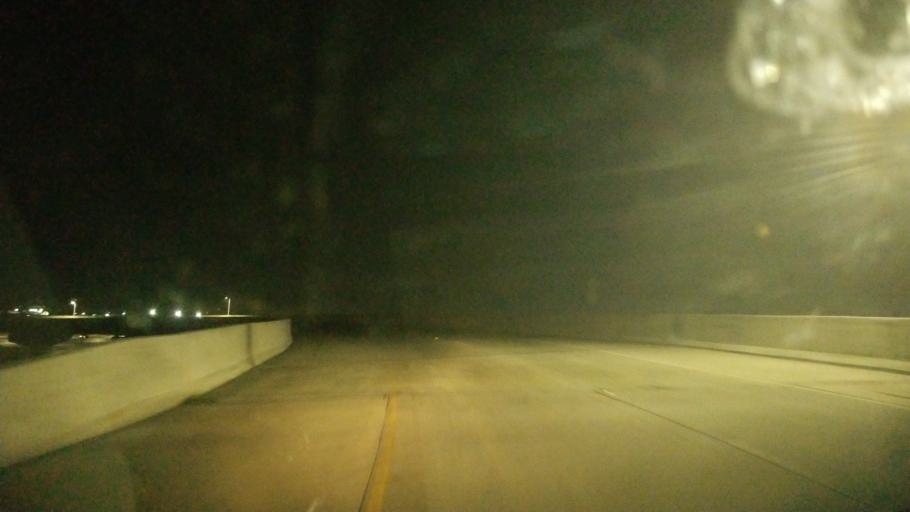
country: US
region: Indiana
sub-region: Marion County
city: Speedway
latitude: 39.7132
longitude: -86.2621
